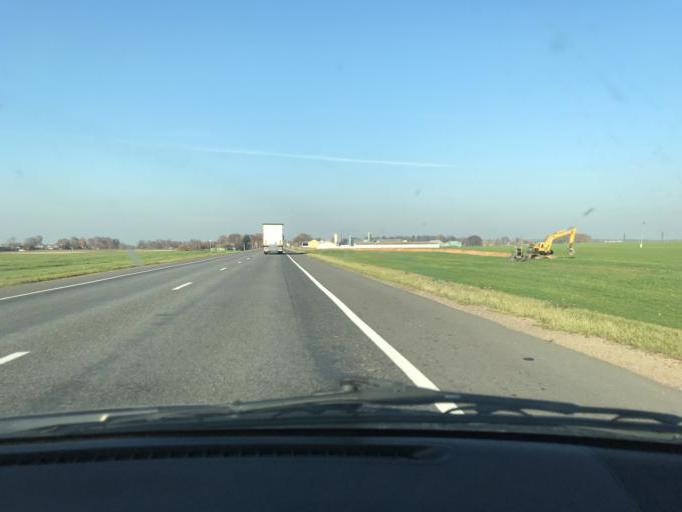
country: BY
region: Mogilev
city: Shklow
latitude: 54.2424
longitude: 30.4511
